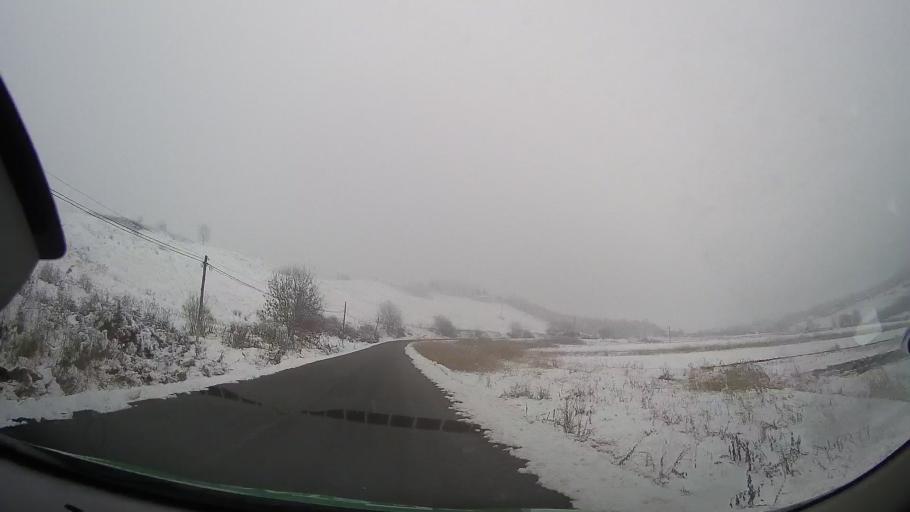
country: RO
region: Bacau
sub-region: Comuna Oncesti
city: Oncesti
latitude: 46.4811
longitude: 27.2573
